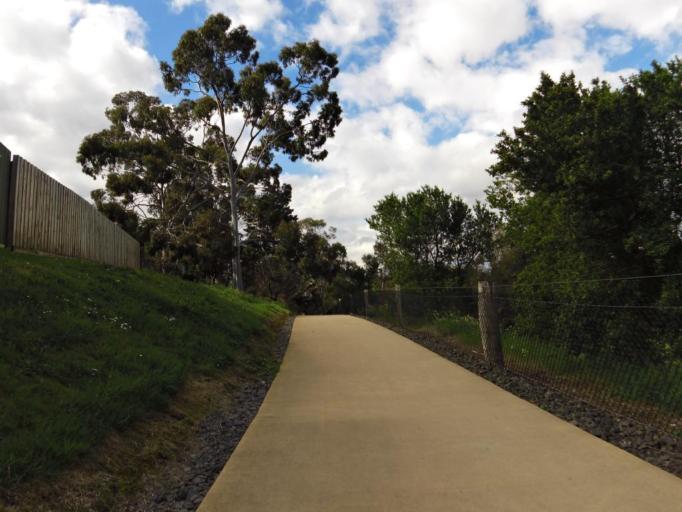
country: AU
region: Victoria
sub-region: Banyule
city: Viewbank
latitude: -37.7501
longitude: 145.0828
